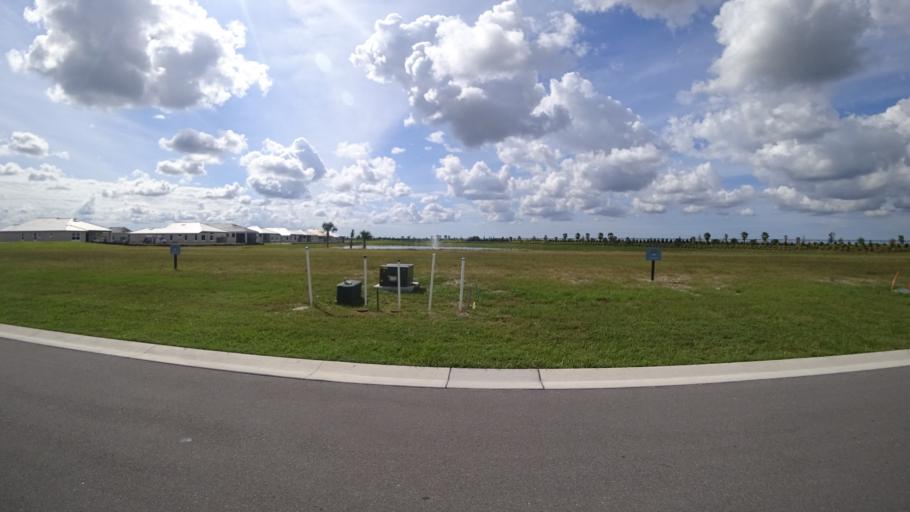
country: US
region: Florida
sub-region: Sarasota County
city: The Meadows
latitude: 27.3993
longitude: -82.3606
